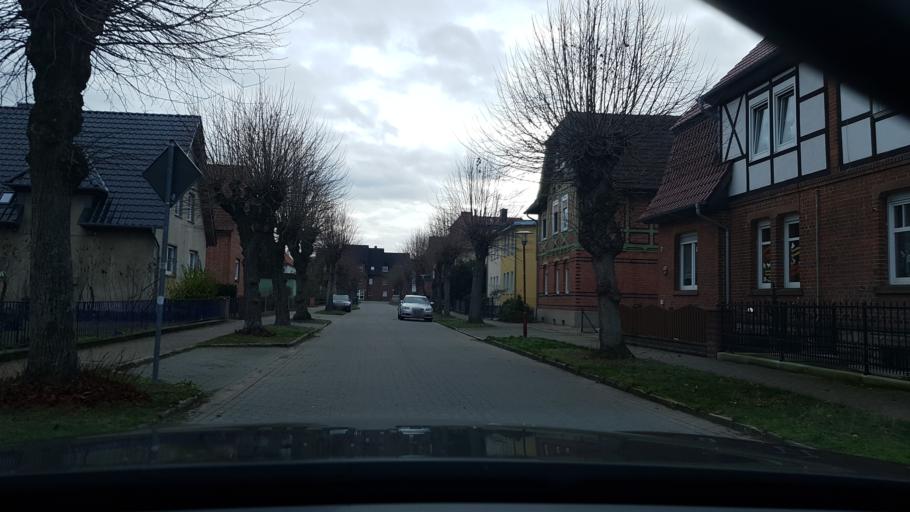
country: DE
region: Saxony-Anhalt
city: Oebisfelde
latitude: 52.4362
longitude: 10.9900
